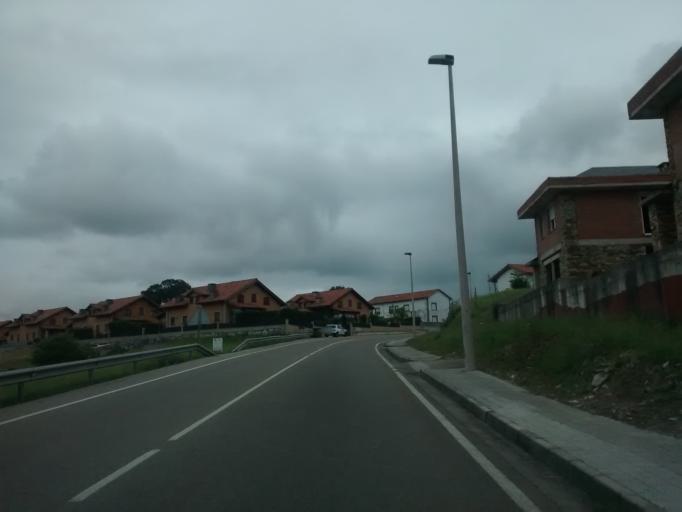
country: ES
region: Cantabria
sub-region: Provincia de Cantabria
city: Polanco
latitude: 43.3898
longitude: -4.0467
